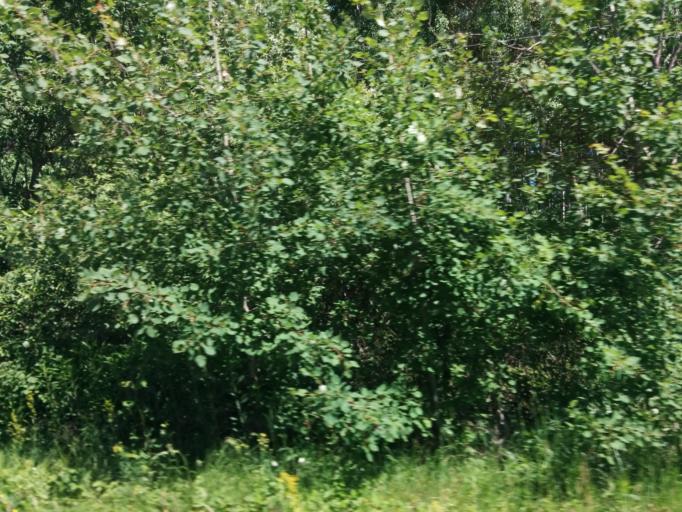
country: RU
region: Tambov
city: Morshansk
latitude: 53.6494
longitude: 41.8508
